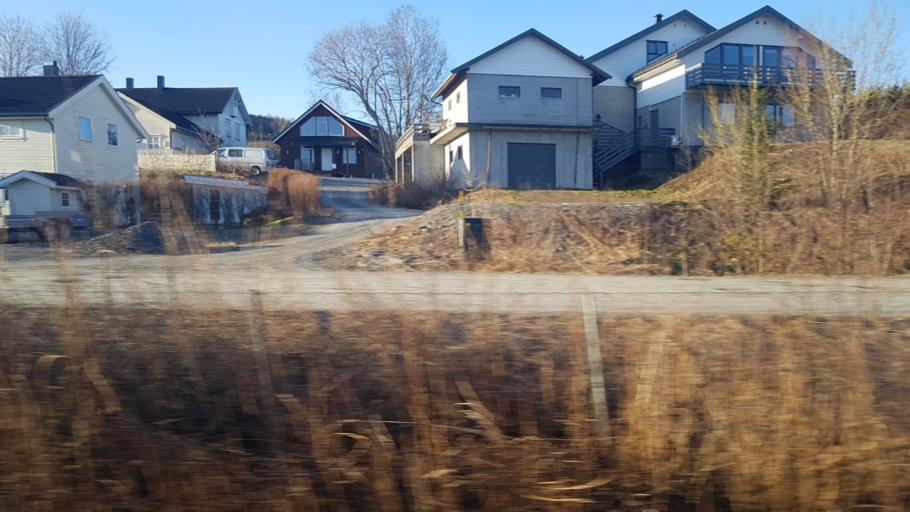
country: NO
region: Sor-Trondelag
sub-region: Malvik
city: Malvik
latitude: 63.4305
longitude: 10.7003
